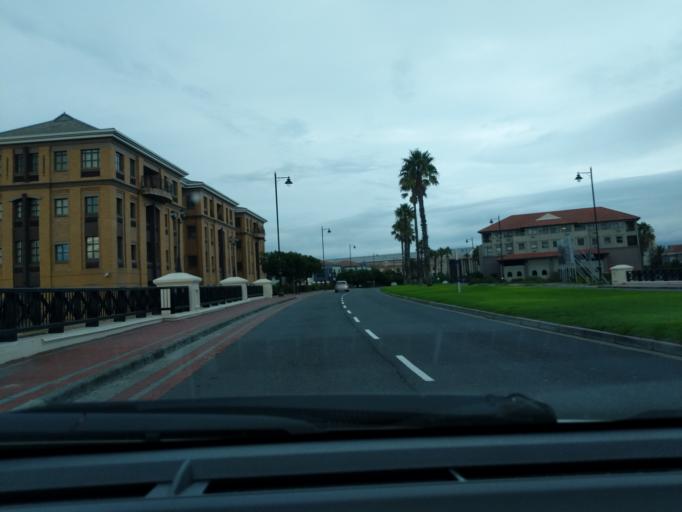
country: ZA
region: Western Cape
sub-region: City of Cape Town
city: Sunset Beach
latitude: -33.8872
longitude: 18.5203
